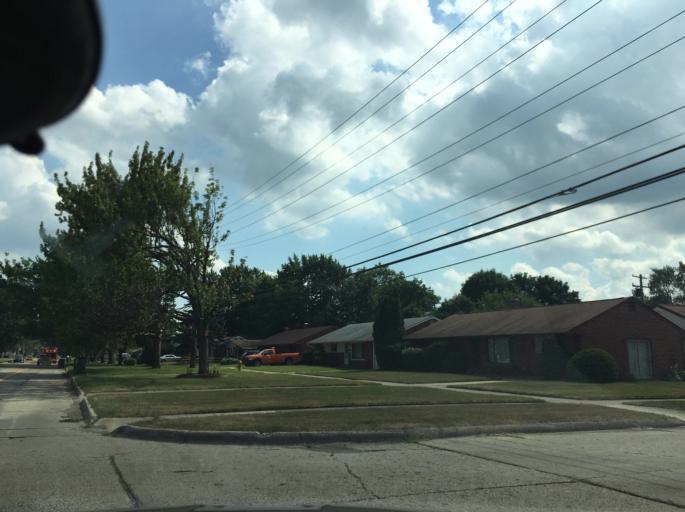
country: US
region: Michigan
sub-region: Macomb County
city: Clinton
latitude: 42.5580
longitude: -82.9105
